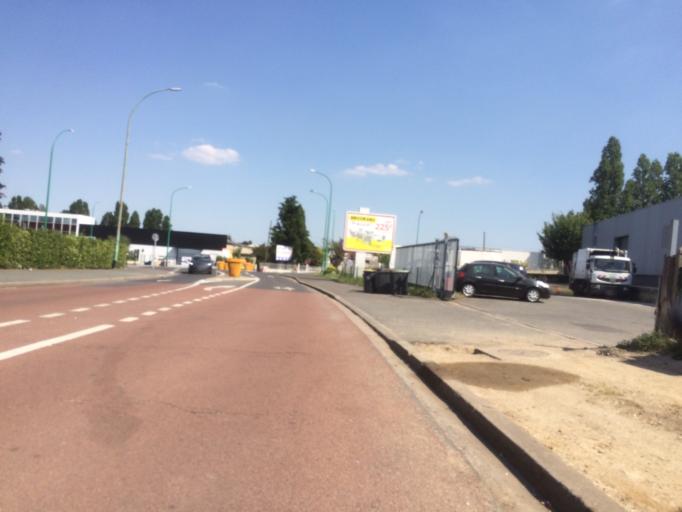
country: FR
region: Ile-de-France
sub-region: Departement de l'Essonne
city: Morangis
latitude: 48.6956
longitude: 2.3353
